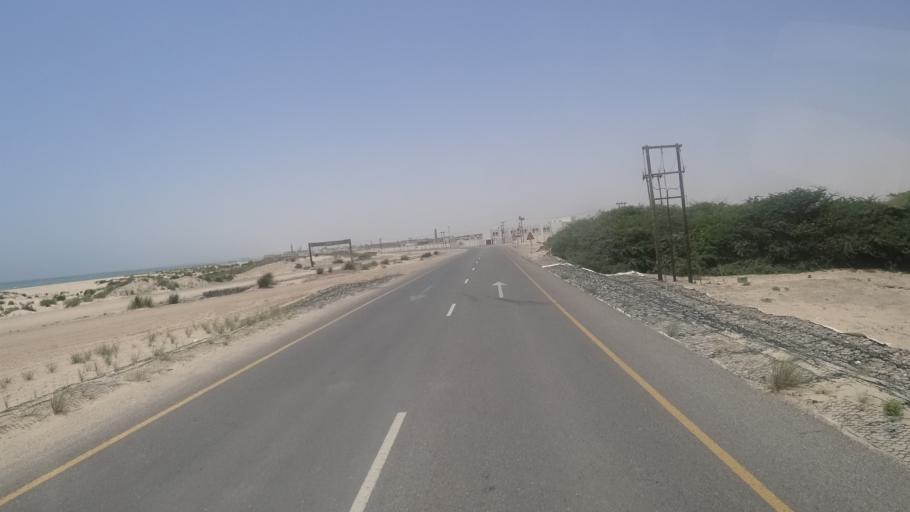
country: OM
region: Ash Sharqiyah
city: Sur
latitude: 22.0910
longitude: 59.6918
